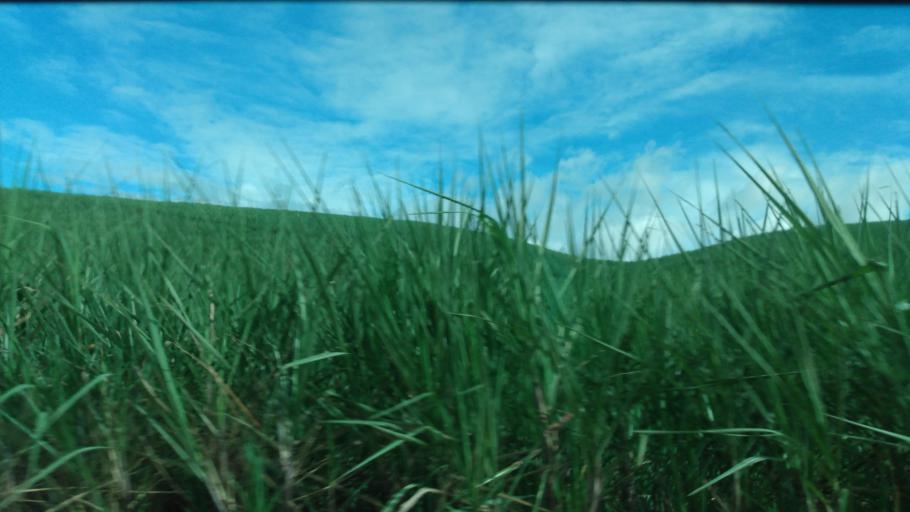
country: BR
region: Pernambuco
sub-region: Palmares
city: Palmares
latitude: -8.6946
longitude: -35.6520
